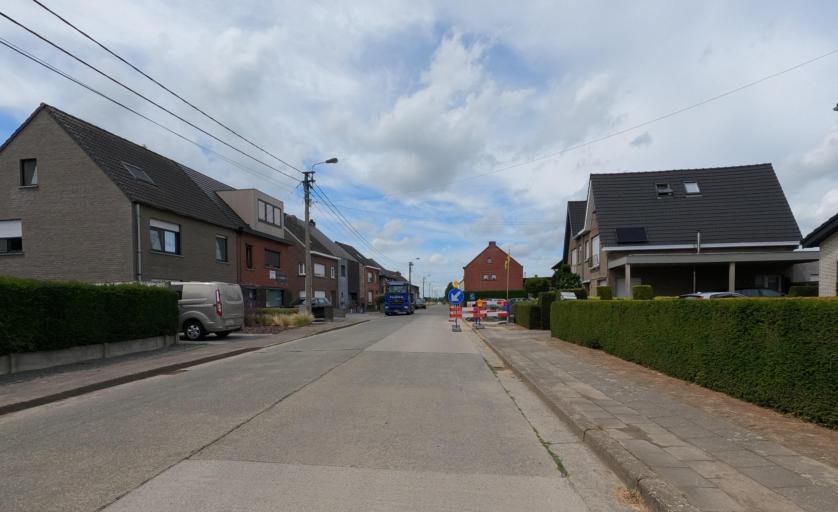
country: BE
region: Flanders
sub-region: Provincie Oost-Vlaanderen
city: Wichelen
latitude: 50.9998
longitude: 3.9487
